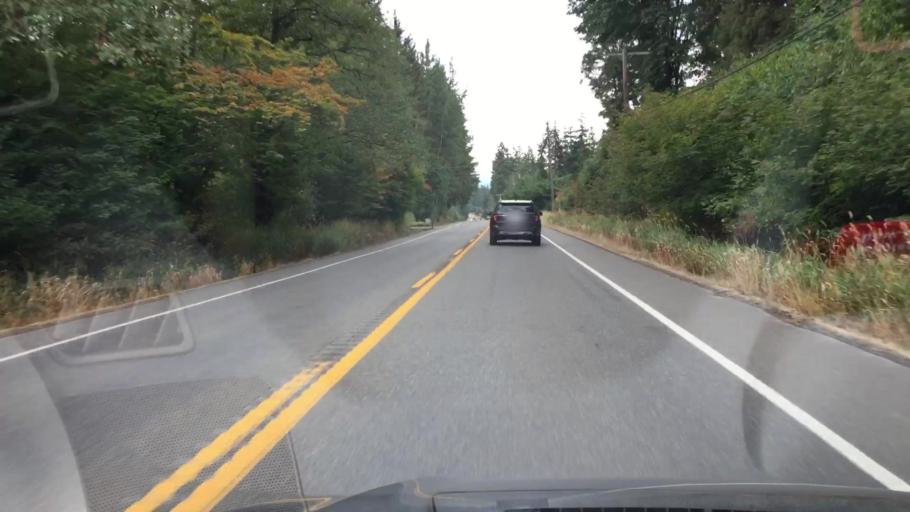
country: US
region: Washington
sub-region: Pierce County
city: Graham
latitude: 47.0102
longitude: -122.2964
